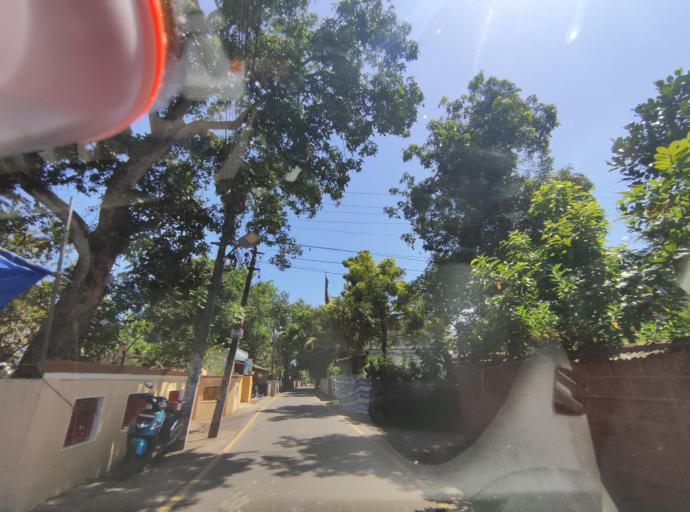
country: IN
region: Kerala
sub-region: Alappuzha
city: Alleppey
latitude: 9.4753
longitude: 76.3311
